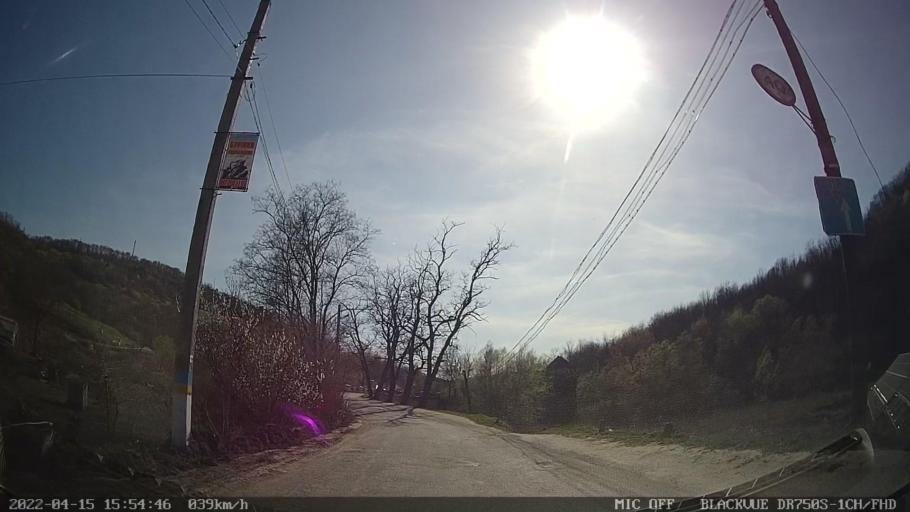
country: MD
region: Raionul Ocnita
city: Otaci
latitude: 48.4026
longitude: 27.8882
